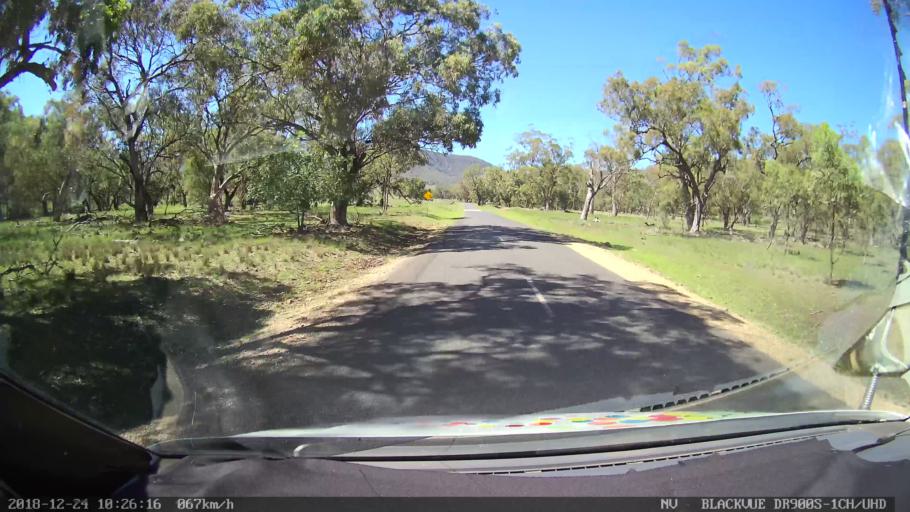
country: AU
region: New South Wales
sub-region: Liverpool Plains
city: Quirindi
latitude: -31.8077
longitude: 150.5278
